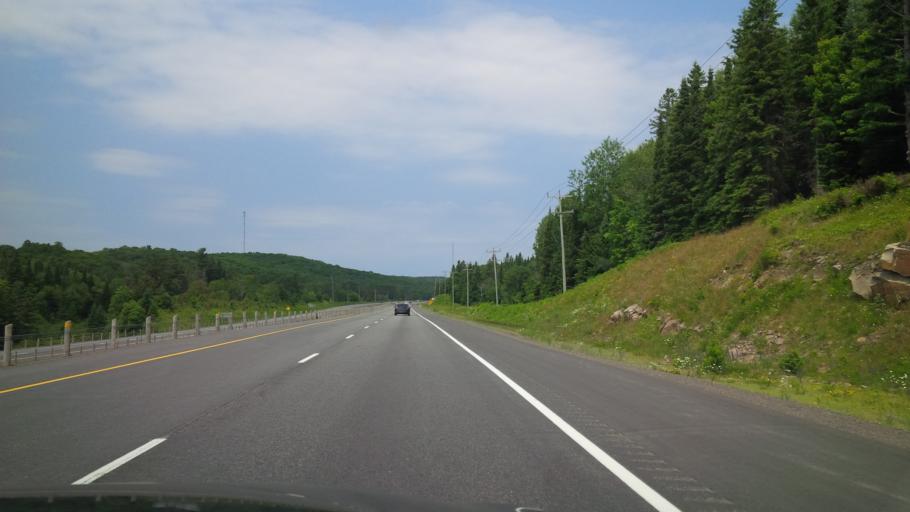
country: CA
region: Ontario
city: Huntsville
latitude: 45.3863
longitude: -79.2285
